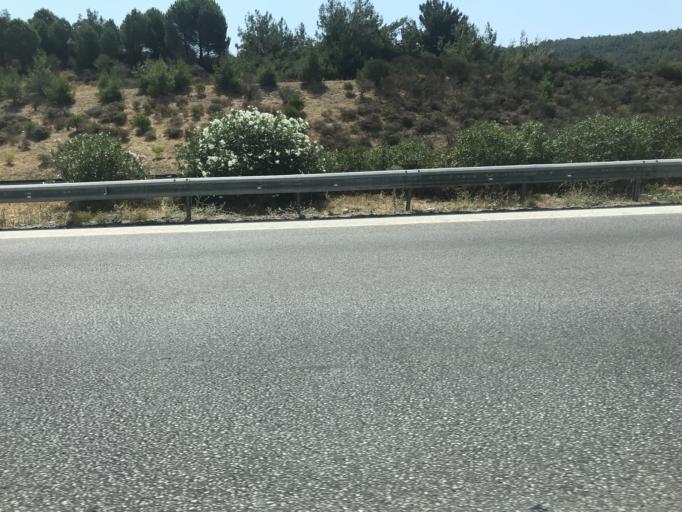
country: TR
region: Izmir
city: Urla
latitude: 38.3205
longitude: 26.7951
